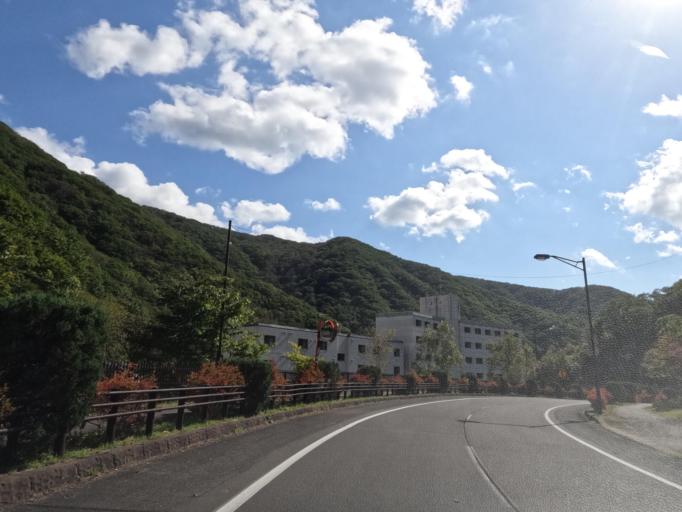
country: JP
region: Hokkaido
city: Shiraoi
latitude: 42.4904
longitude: 141.1448
